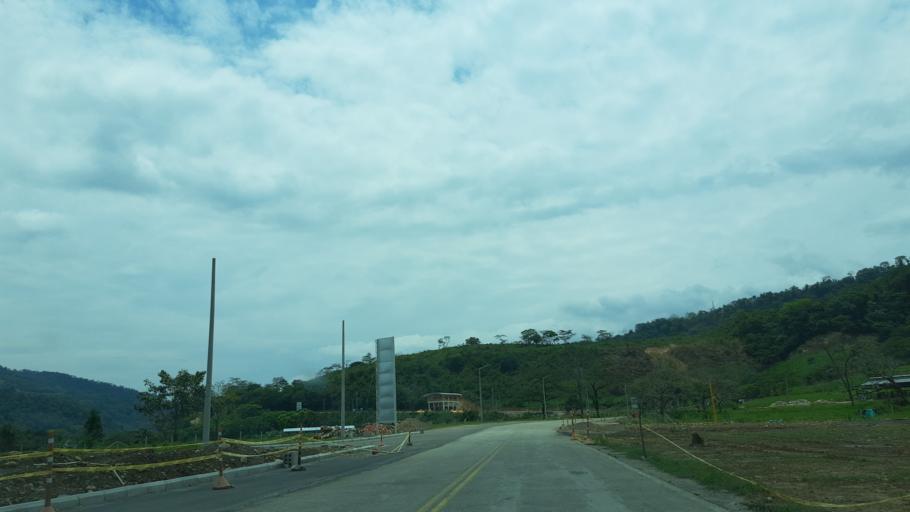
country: CO
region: Casanare
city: Sabanalarga
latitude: 4.8244
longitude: -73.0796
